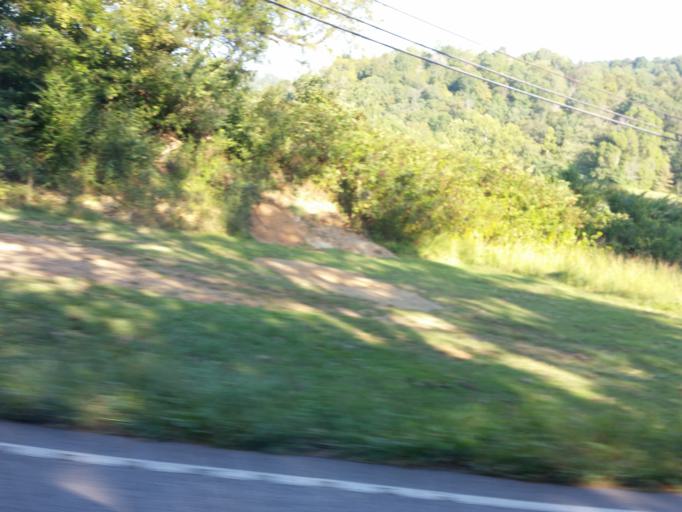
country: US
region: Tennessee
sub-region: Union County
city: Luttrell
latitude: 36.2405
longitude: -83.7466
